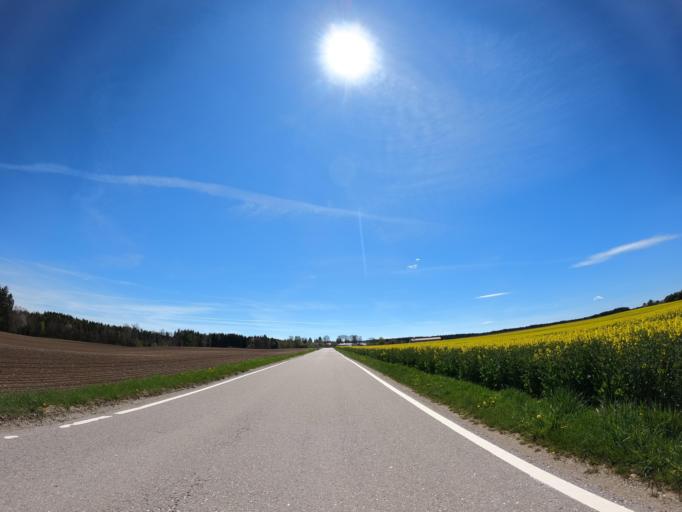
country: DE
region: Bavaria
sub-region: Upper Bavaria
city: Strasslach-Dingharting
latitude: 47.9977
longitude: 11.5580
